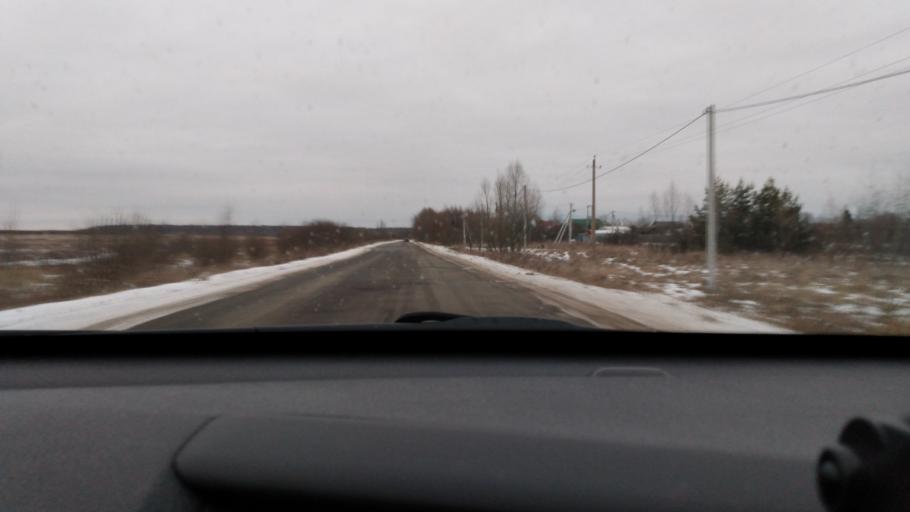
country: RU
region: Moskovskaya
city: Meshcherino
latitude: 55.2963
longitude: 38.3429
